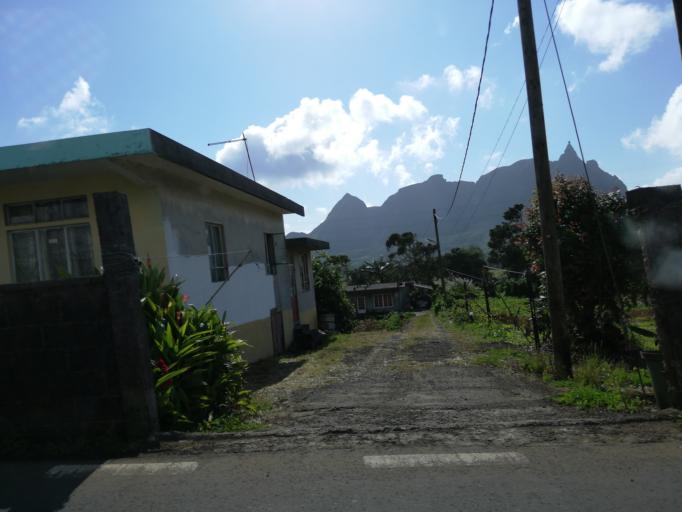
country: MU
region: Pamplemousses
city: Creve Coeur
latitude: -20.2078
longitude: 57.5666
